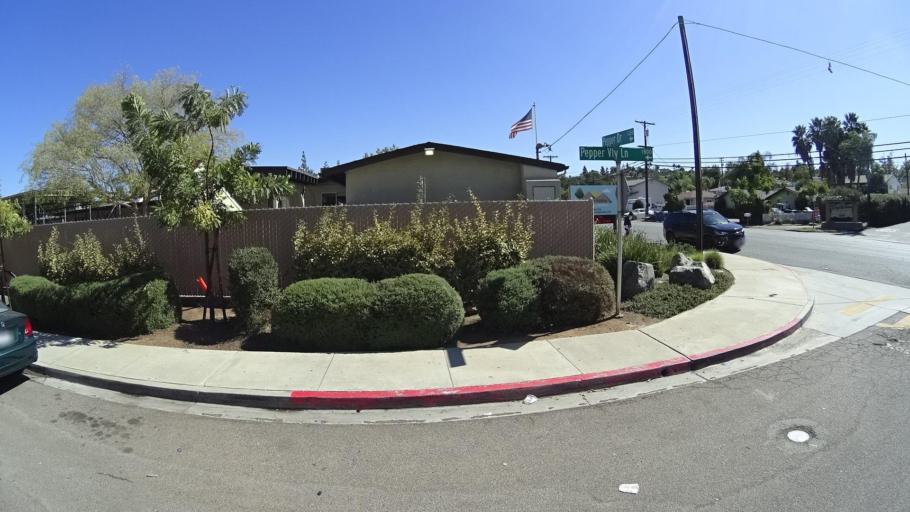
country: US
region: California
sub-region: San Diego County
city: Winter Gardens
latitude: 32.8211
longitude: -116.9319
